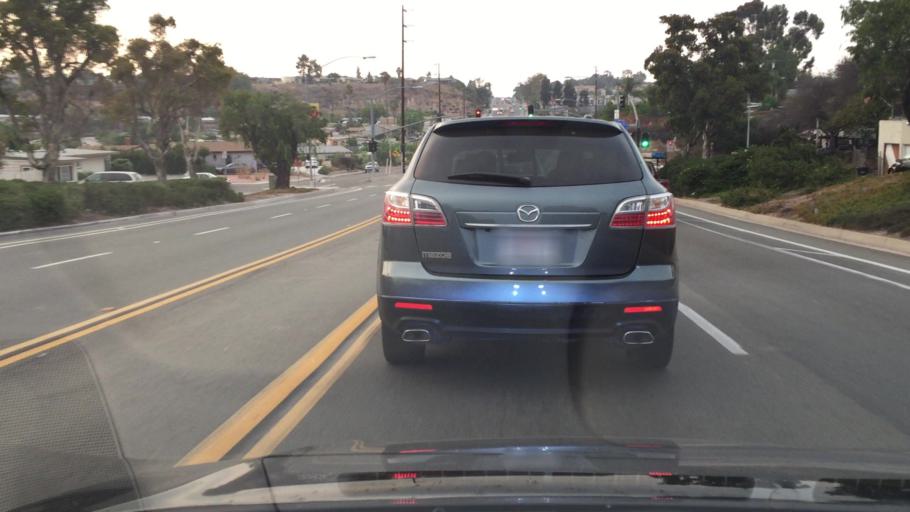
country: US
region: California
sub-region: San Diego County
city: Lemon Grove
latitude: 32.7421
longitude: -117.0795
